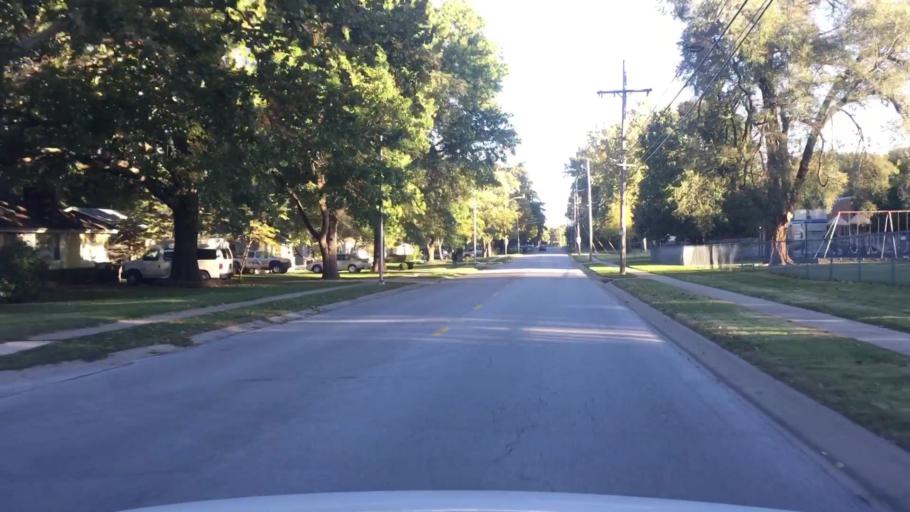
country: US
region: Kansas
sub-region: Johnson County
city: Mission
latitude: 39.0087
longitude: -94.6722
